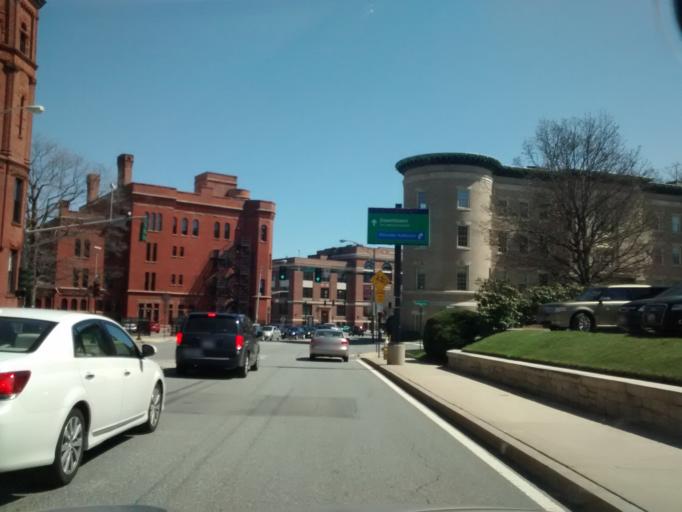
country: US
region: Massachusetts
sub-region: Worcester County
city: Worcester
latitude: 42.2738
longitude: -71.8018
